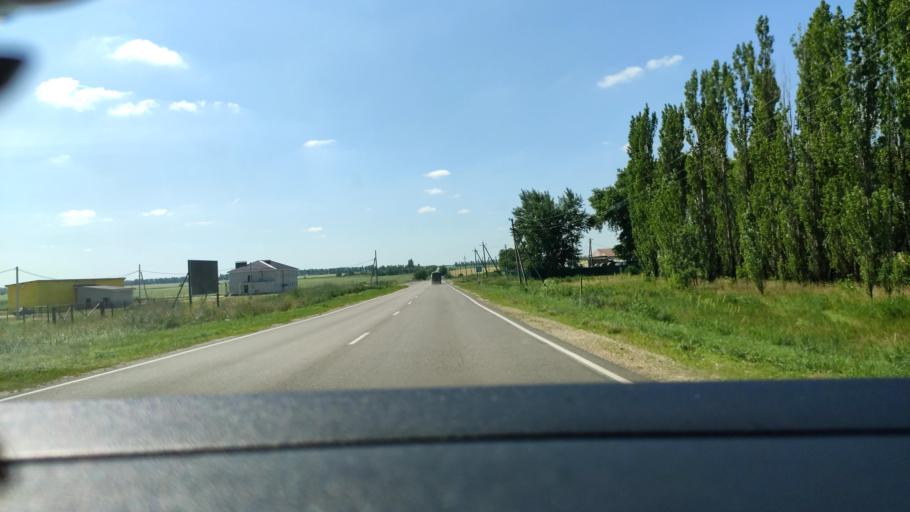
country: RU
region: Voronezj
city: Novaya Usman'
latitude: 51.5831
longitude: 39.3746
